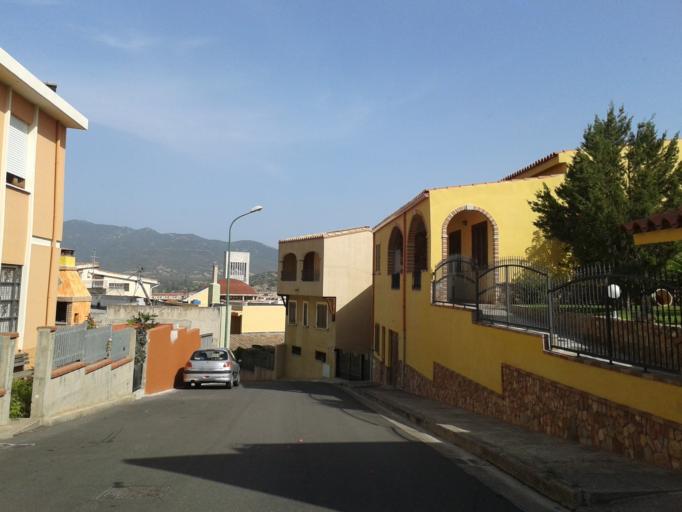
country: IT
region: Sardinia
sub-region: Provincia di Cagliari
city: Villasimius
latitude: 39.1409
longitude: 9.5201
